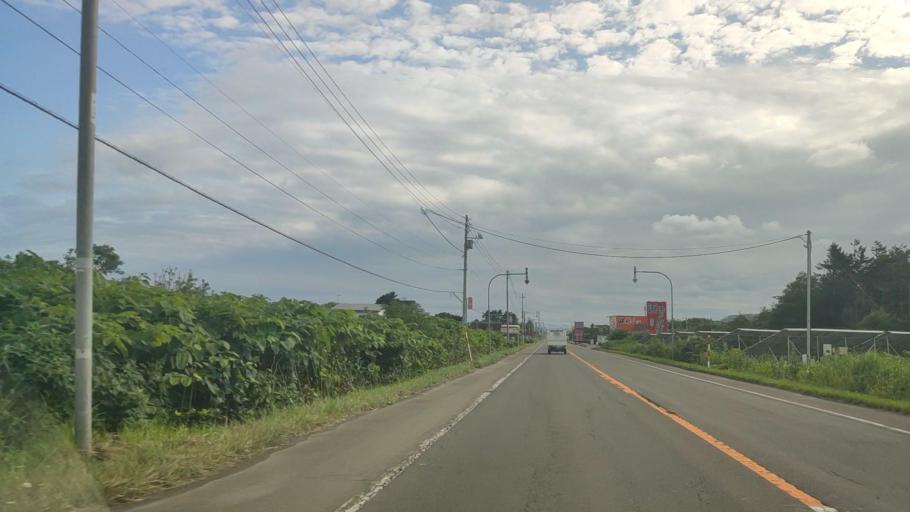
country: JP
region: Hokkaido
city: Niseko Town
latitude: 42.4807
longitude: 140.3503
